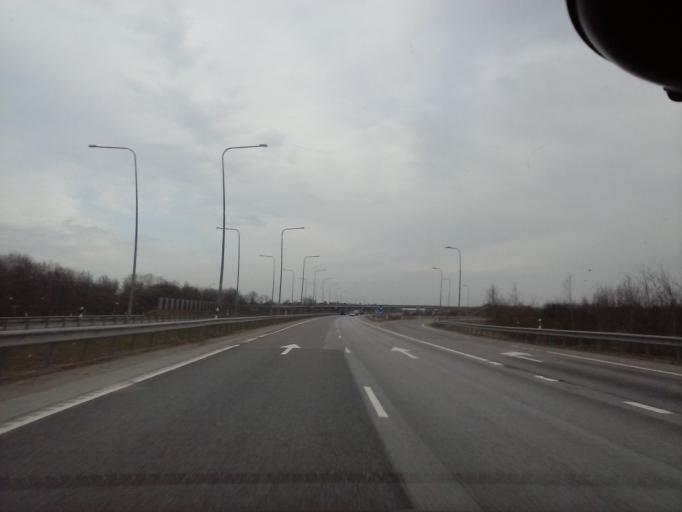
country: EE
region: Harju
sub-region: Rae vald
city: Vaida
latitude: 59.2944
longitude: 24.9600
